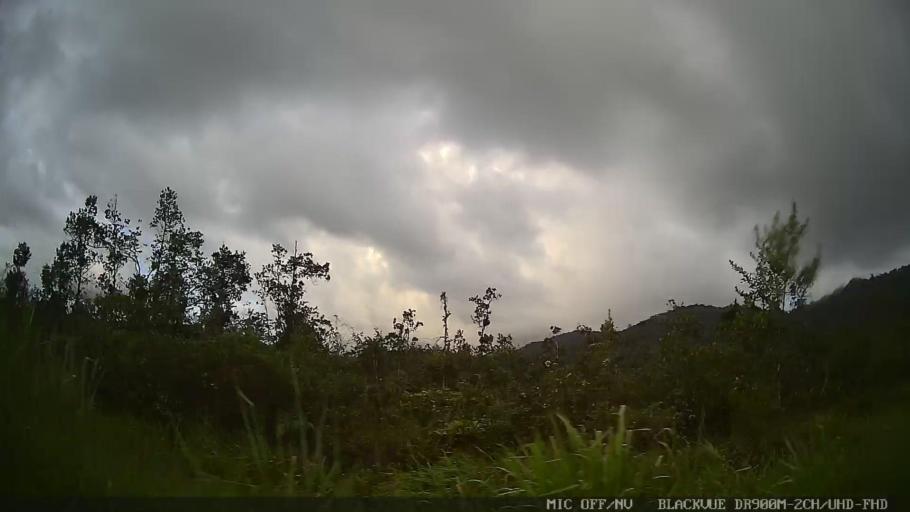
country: BR
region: Sao Paulo
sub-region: Itanhaem
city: Itanhaem
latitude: -24.1357
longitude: -46.7781
